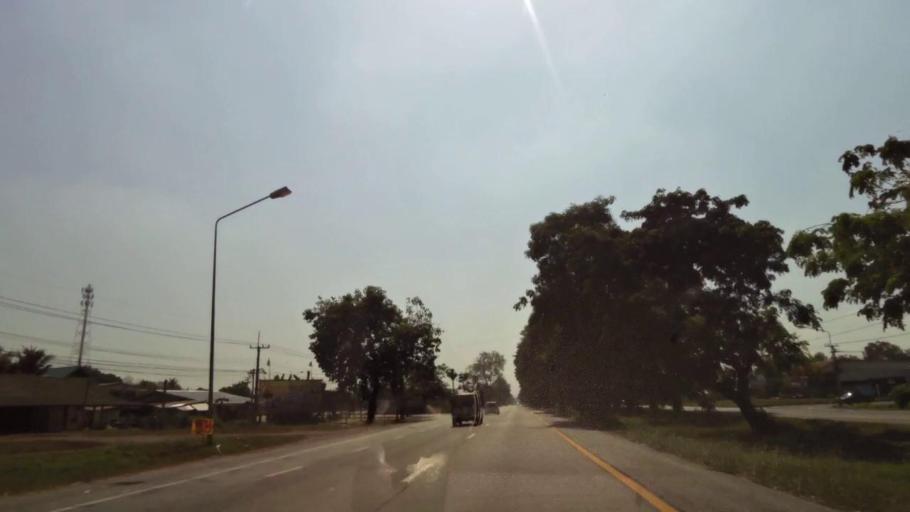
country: TH
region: Phichit
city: Wachira Barami
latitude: 16.6355
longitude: 100.1496
